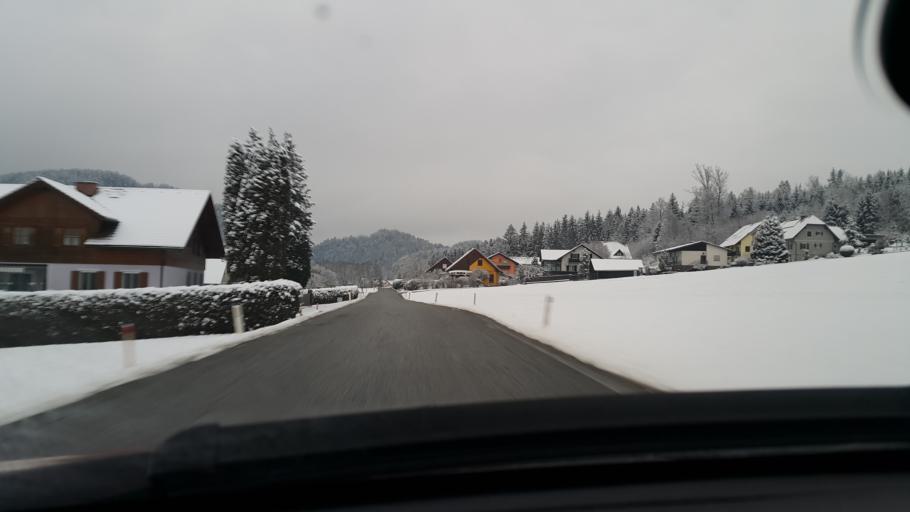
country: AT
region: Styria
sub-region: Politischer Bezirk Graz-Umgebung
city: Sankt Oswald bei Plankenwarth
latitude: 47.0776
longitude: 15.2628
